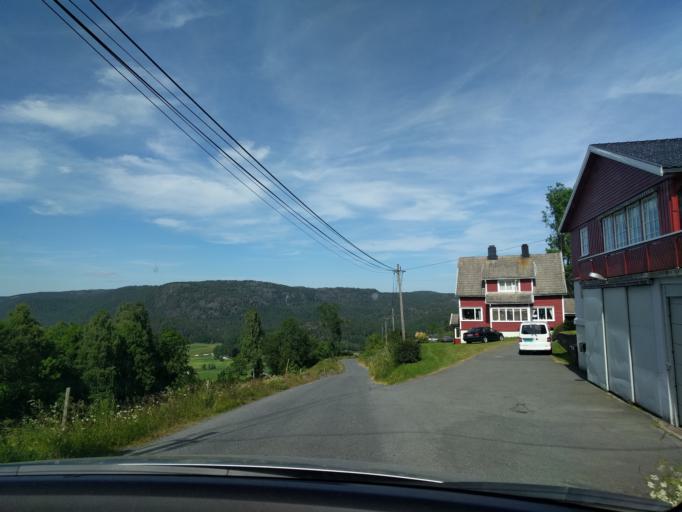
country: NO
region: Aust-Agder
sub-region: Gjerstad
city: Gjerstad
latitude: 58.8877
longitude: 8.9594
